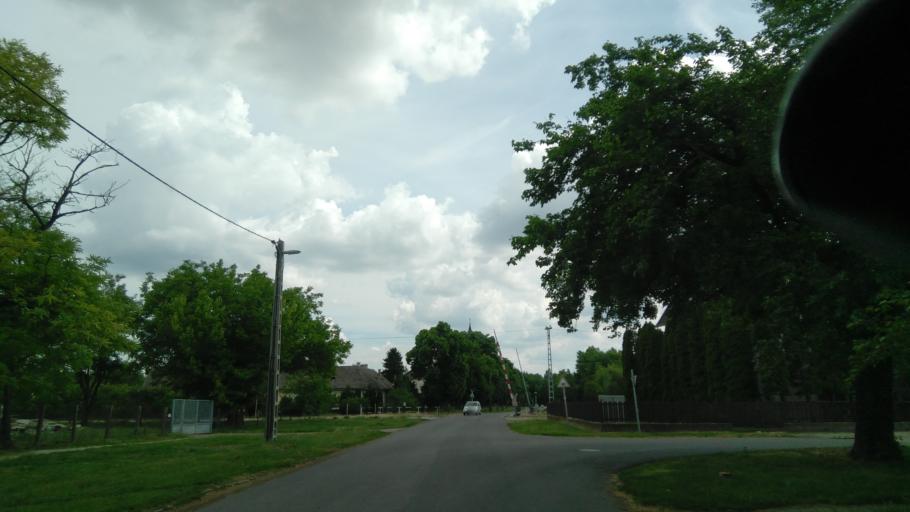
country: HU
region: Bekes
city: Mezohegyes
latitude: 46.3135
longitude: 20.8233
